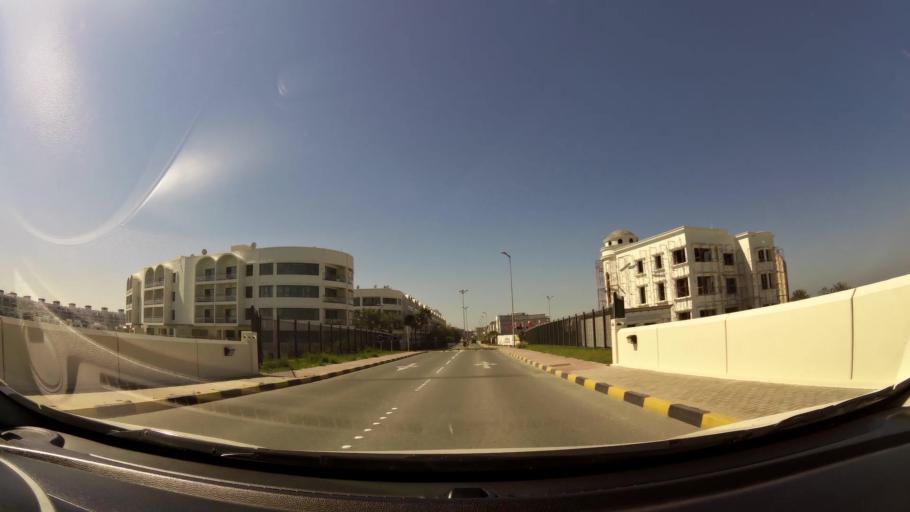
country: BH
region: Muharraq
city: Al Hadd
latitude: 26.2989
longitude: 50.6668
